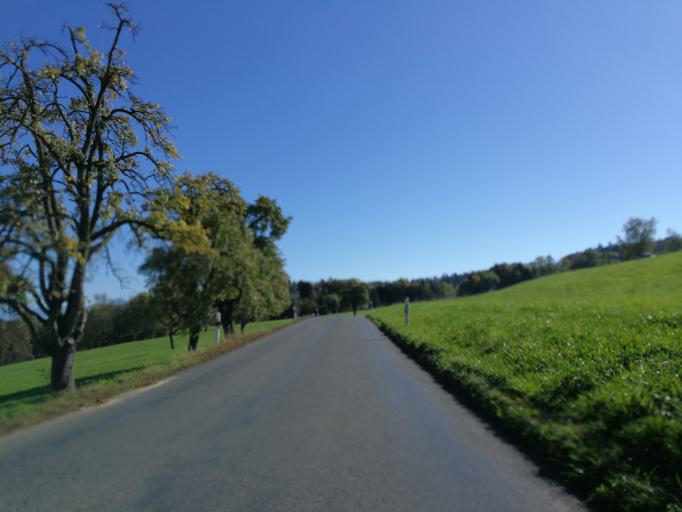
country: CH
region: Zurich
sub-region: Bezirk Uster
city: Esslingen
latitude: 47.2811
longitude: 8.6987
